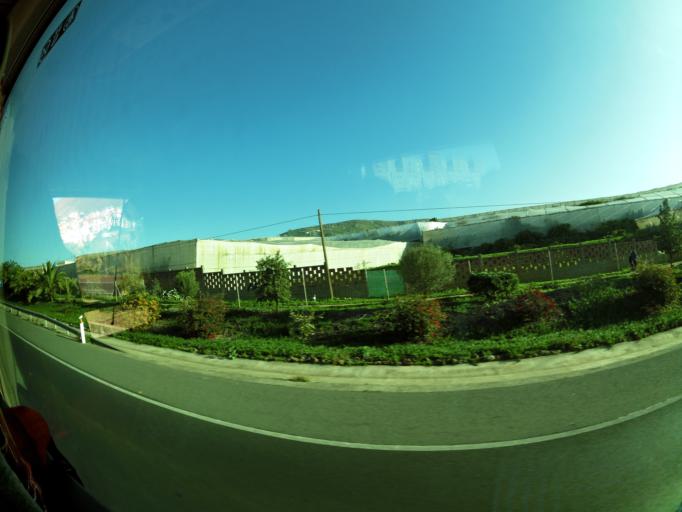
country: ES
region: Canary Islands
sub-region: Provincia de Las Palmas
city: Galdar
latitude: 28.1422
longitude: -15.6479
